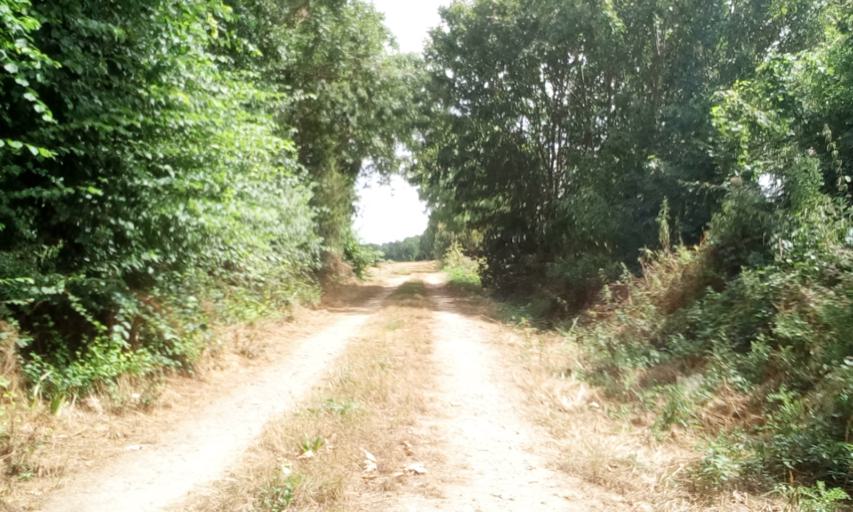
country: FR
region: Lower Normandy
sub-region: Departement du Calvados
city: Troarn
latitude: 49.1734
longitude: -0.2012
